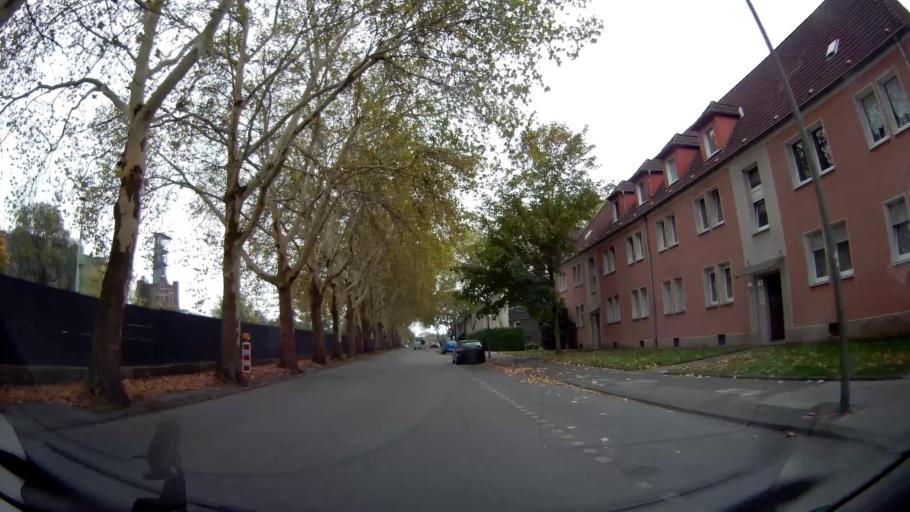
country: DE
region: North Rhine-Westphalia
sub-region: Regierungsbezirk Munster
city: Bottrop
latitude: 51.5204
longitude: 6.9567
